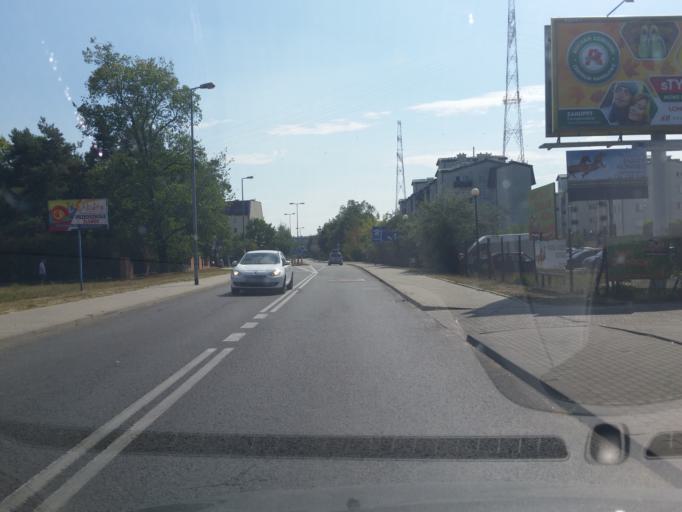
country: PL
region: Masovian Voivodeship
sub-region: Warszawa
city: Bialoleka
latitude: 52.3290
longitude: 20.9362
